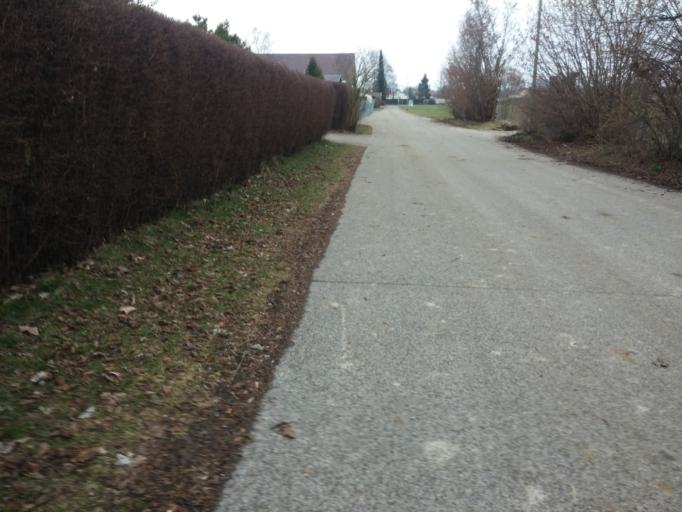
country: DE
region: Bavaria
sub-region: Swabia
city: Buxheim
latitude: 47.9953
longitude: 10.1552
